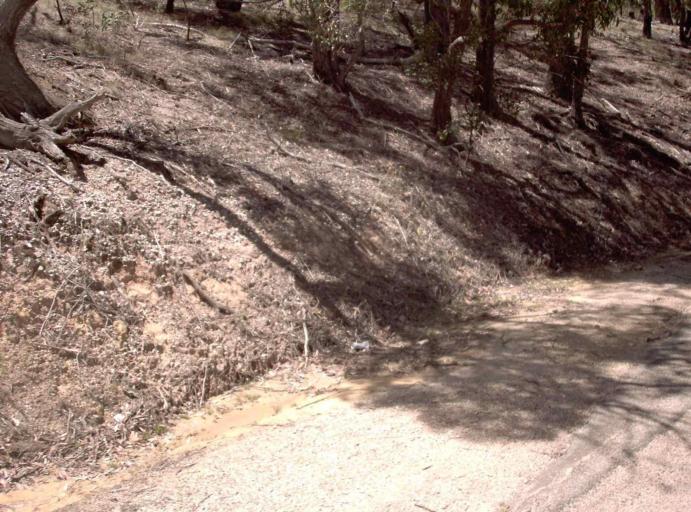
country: AU
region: Victoria
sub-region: East Gippsland
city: Lakes Entrance
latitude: -37.6291
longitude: 147.8880
